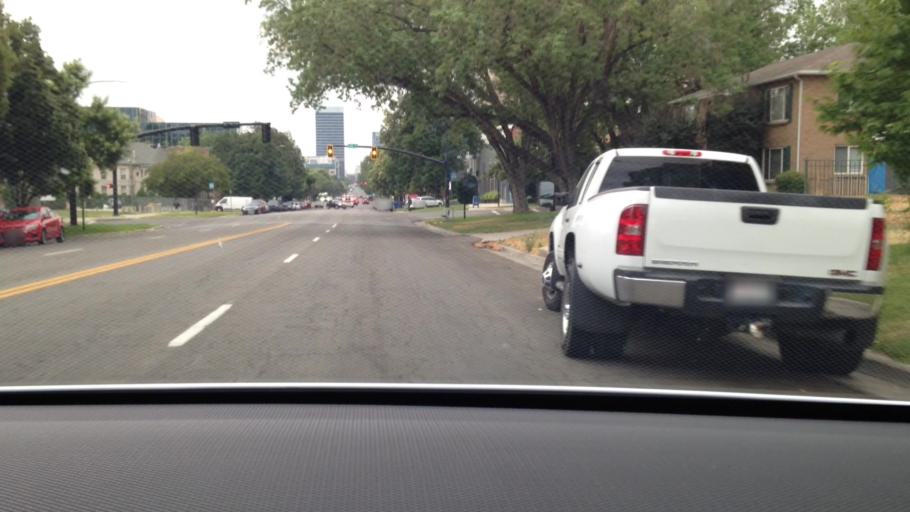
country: US
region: Utah
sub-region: Salt Lake County
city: Salt Lake City
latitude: 40.7673
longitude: -111.8729
